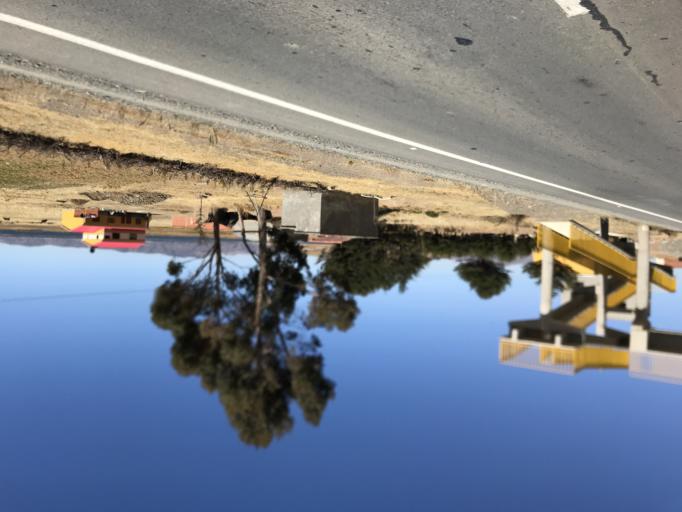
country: BO
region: La Paz
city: Huarina
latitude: -16.2104
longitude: -68.5924
